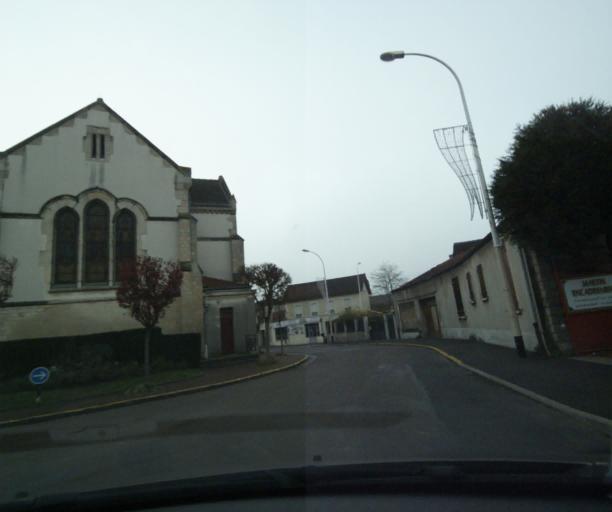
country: FR
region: Ile-de-France
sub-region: Departement de Seine-Saint-Denis
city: Neuilly-Plaisance
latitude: 48.8574
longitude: 2.5078
